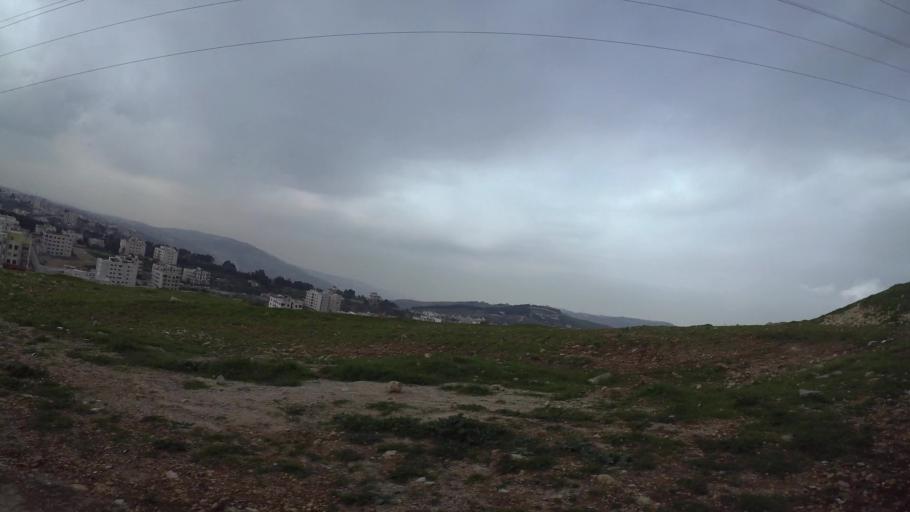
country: JO
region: Amman
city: Umm as Summaq
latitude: 31.9029
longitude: 35.8322
